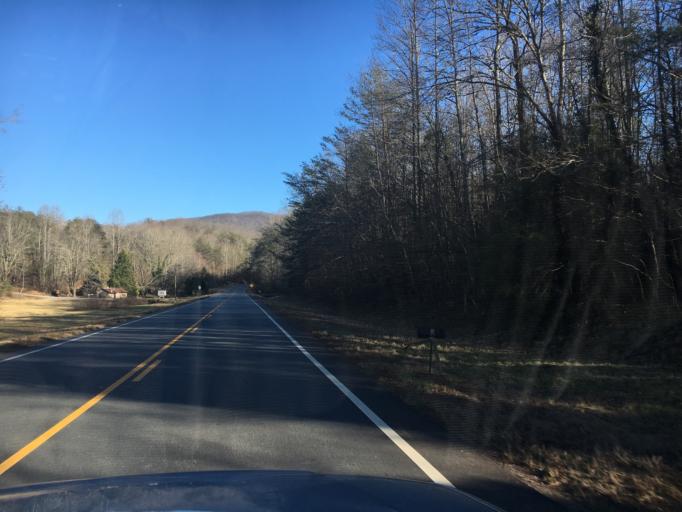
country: US
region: Georgia
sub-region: White County
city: Cleveland
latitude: 34.6686
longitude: -83.8639
